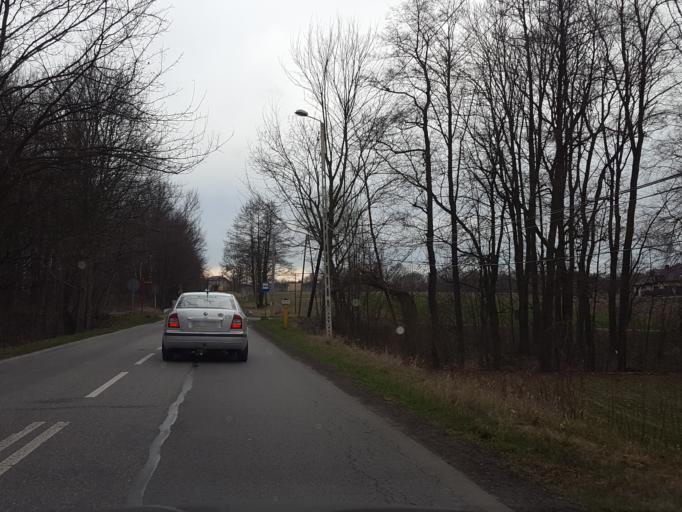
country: PL
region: Silesian Voivodeship
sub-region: Powiat gliwicki
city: Paniowki
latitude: 50.2055
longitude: 18.8102
